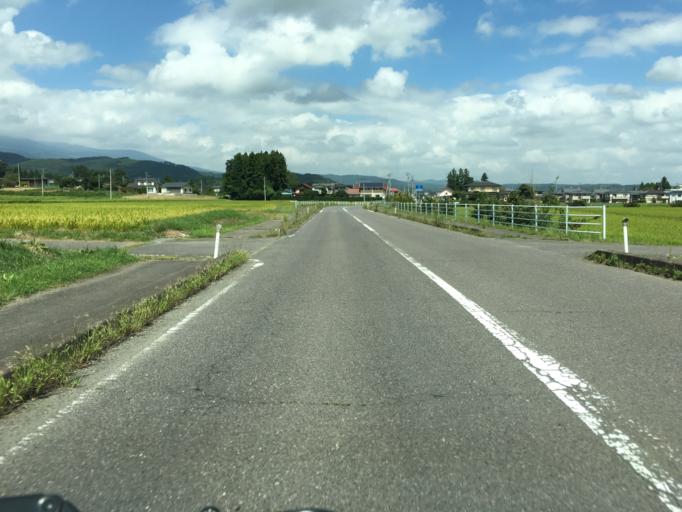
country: JP
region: Fukushima
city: Motomiya
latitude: 37.5418
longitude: 140.3842
